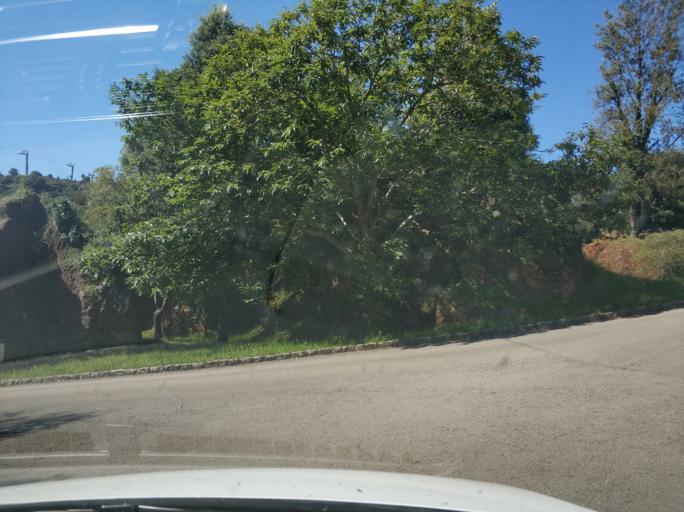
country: ES
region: Cantabria
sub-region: Provincia de Cantabria
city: Penagos
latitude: 43.3624
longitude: -3.8319
